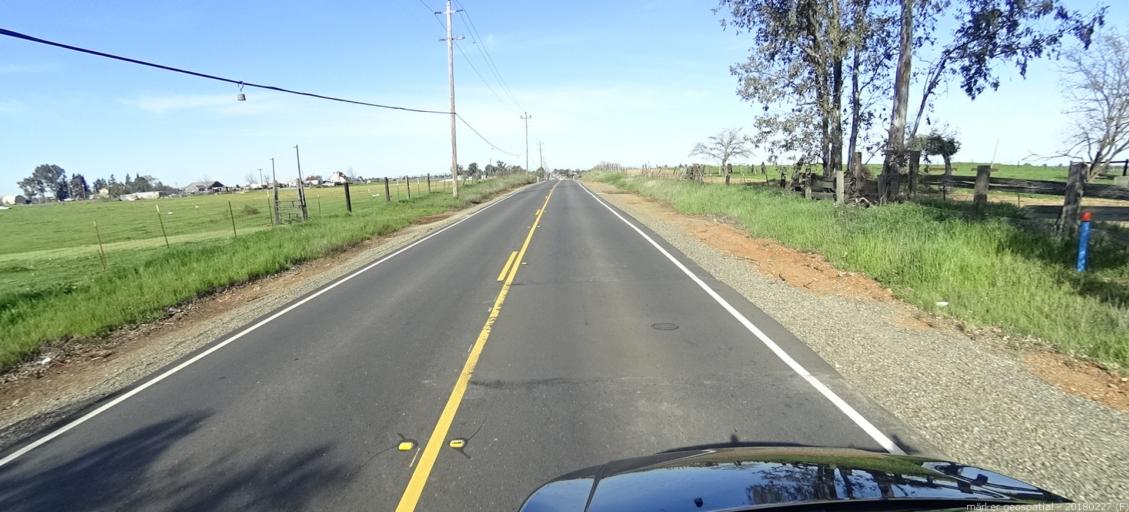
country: US
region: California
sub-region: Sacramento County
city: Vineyard
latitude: 38.4964
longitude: -121.3046
